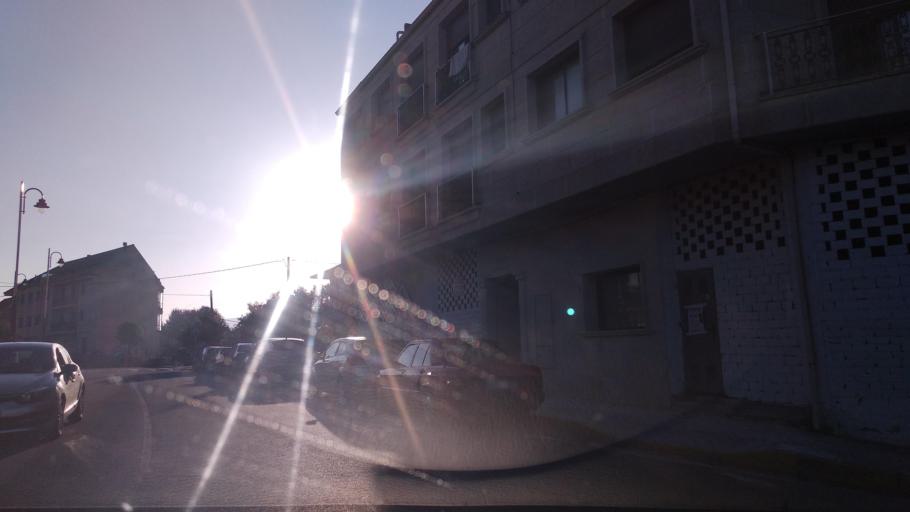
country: ES
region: Galicia
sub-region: Provincia de Pontevedra
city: Redondela
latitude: 42.3393
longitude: -8.5678
